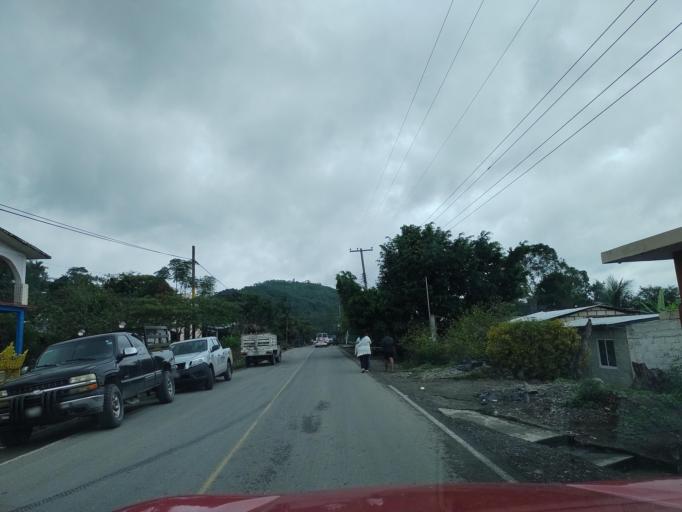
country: MX
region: Puebla
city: Espinal
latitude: 20.2608
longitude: -97.3741
